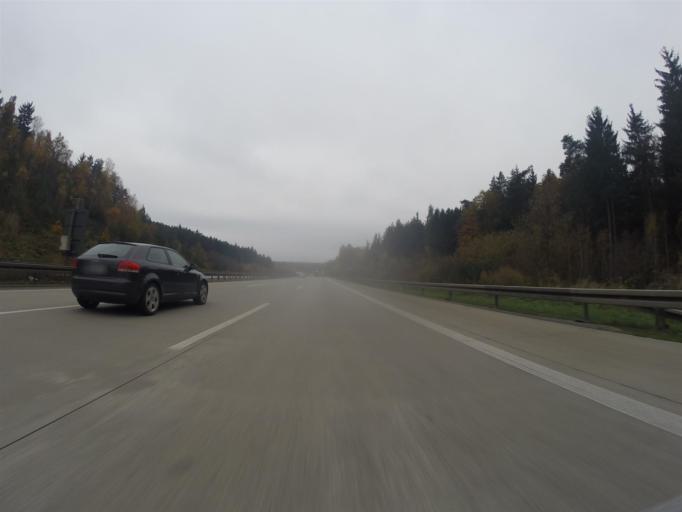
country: DE
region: Thuringia
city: Hainspitz
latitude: 50.9518
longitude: 11.8367
